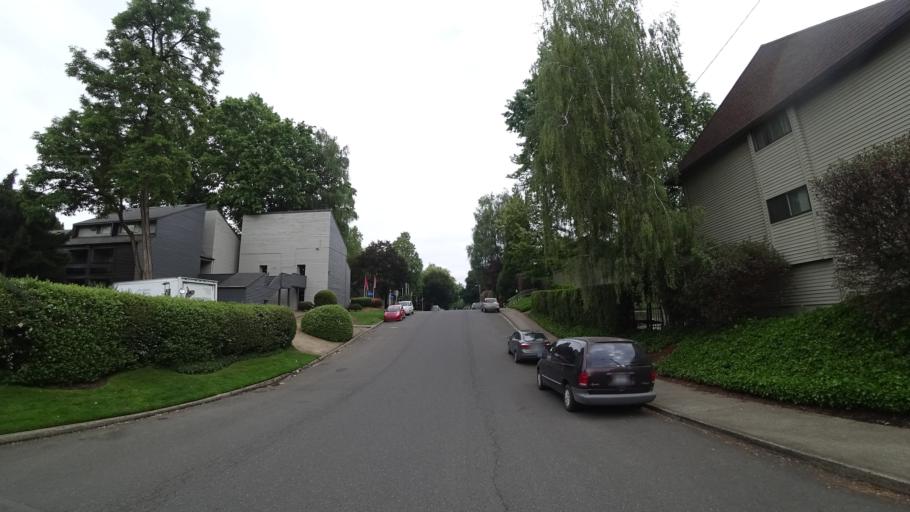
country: US
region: Oregon
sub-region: Clackamas County
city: Milwaukie
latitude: 45.4857
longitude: -122.6344
